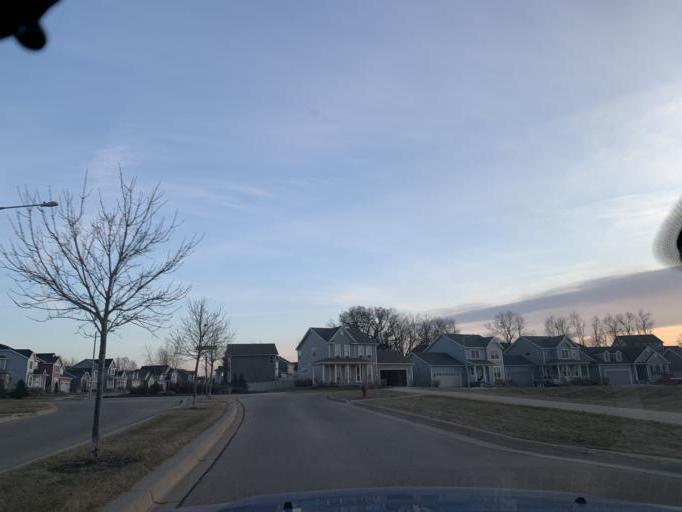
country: US
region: Wisconsin
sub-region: Dane County
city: Middleton
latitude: 43.0581
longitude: -89.5634
